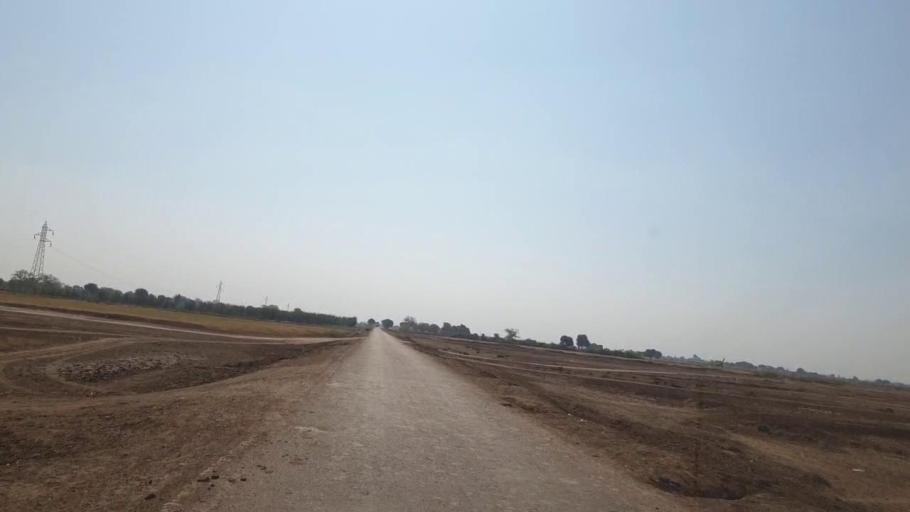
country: PK
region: Sindh
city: Kunri
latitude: 25.1694
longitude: 69.5448
